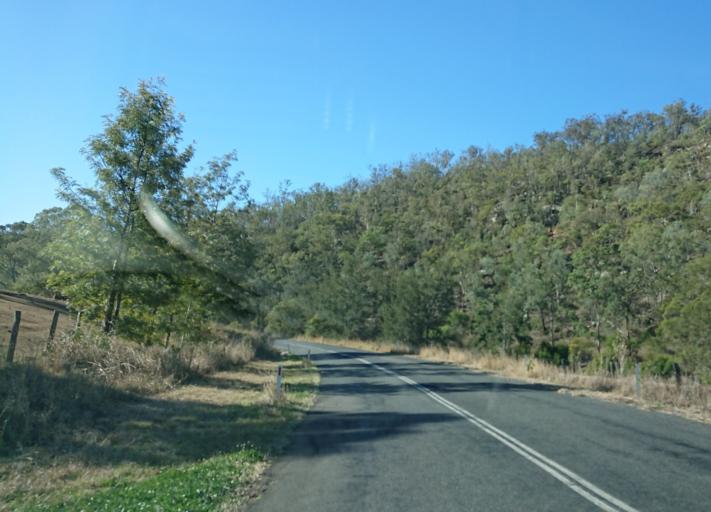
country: AU
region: Queensland
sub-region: Toowoomba
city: Top Camp
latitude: -27.7570
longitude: 152.0827
